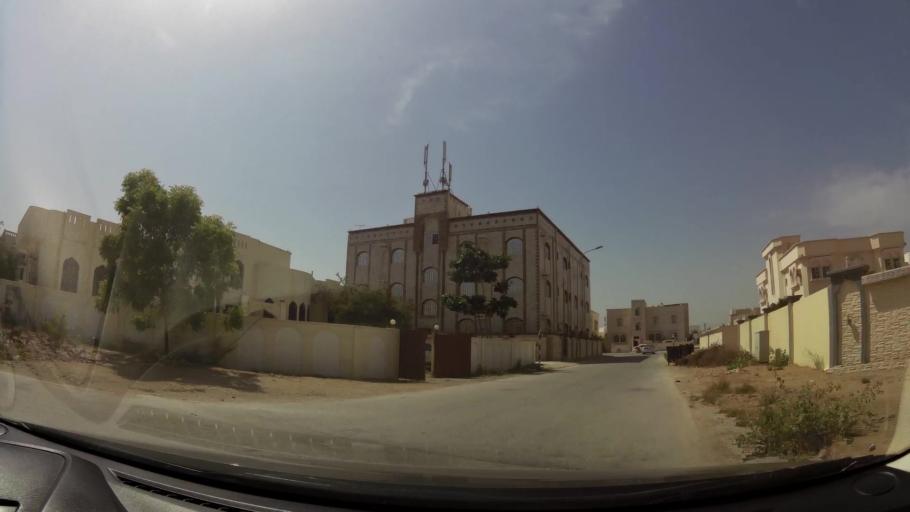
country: OM
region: Zufar
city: Salalah
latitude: 17.0417
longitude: 54.1589
